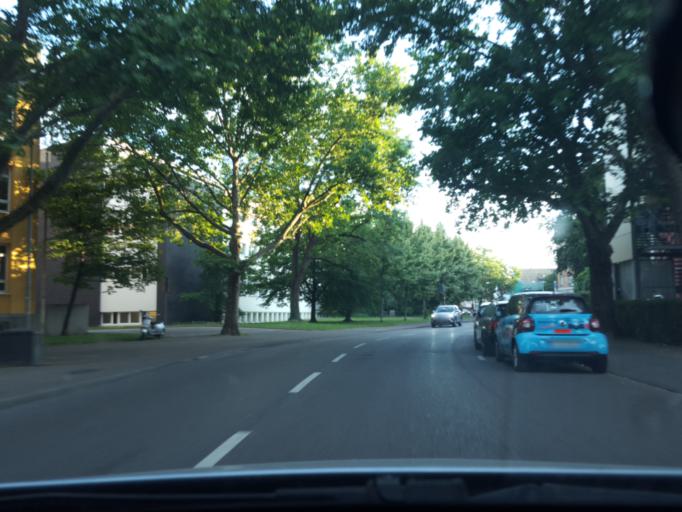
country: DE
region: Baden-Wuerttemberg
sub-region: Regierungsbezirk Stuttgart
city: Stuttgart-Ost
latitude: 48.8078
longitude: 9.2176
